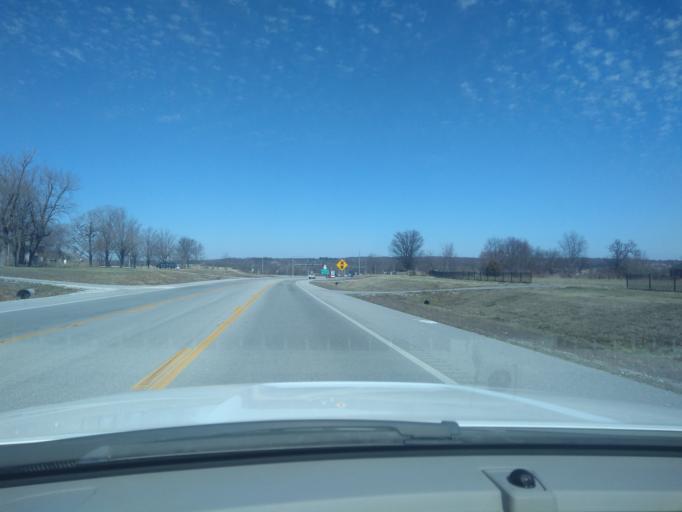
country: US
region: Arkansas
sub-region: Washington County
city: Prairie Grove
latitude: 35.9824
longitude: -94.2995
